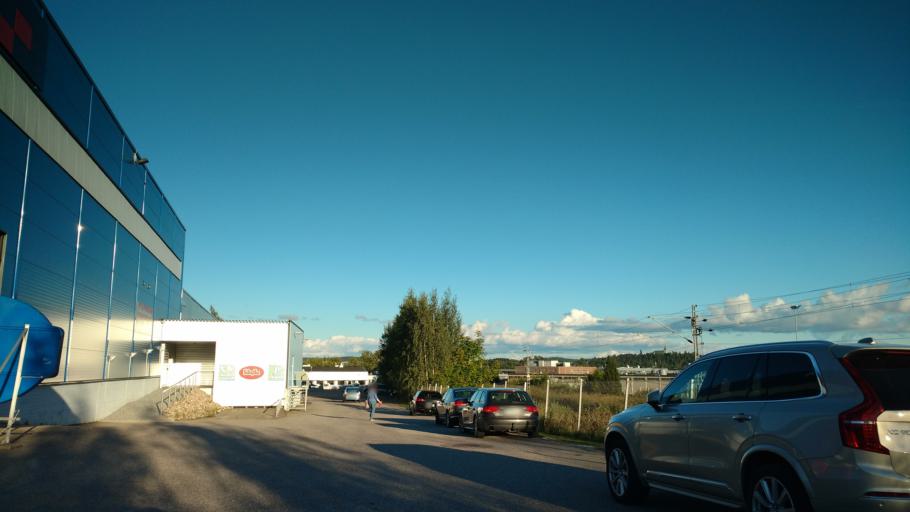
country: FI
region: Varsinais-Suomi
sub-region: Salo
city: Halikko
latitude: 60.3915
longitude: 23.1071
